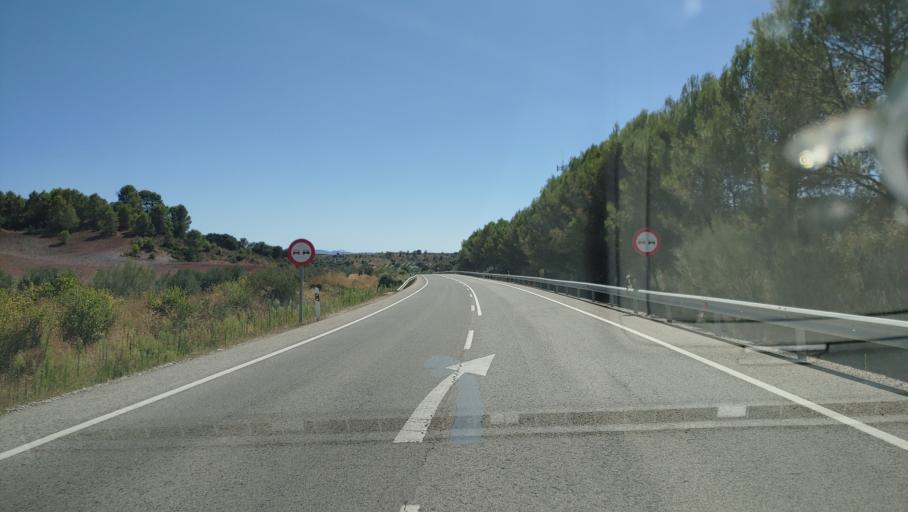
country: ES
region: Andalusia
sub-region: Provincia de Jaen
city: Genave
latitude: 38.4581
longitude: -2.7672
